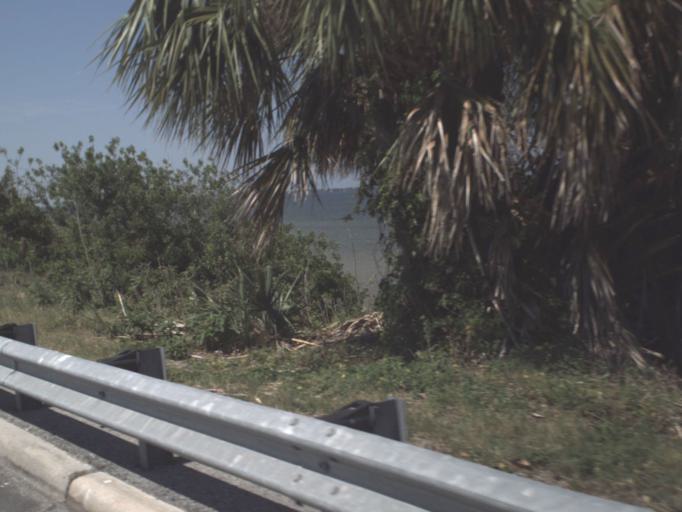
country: US
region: Florida
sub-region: Brevard County
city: Melbourne
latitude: 28.0917
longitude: -80.6089
